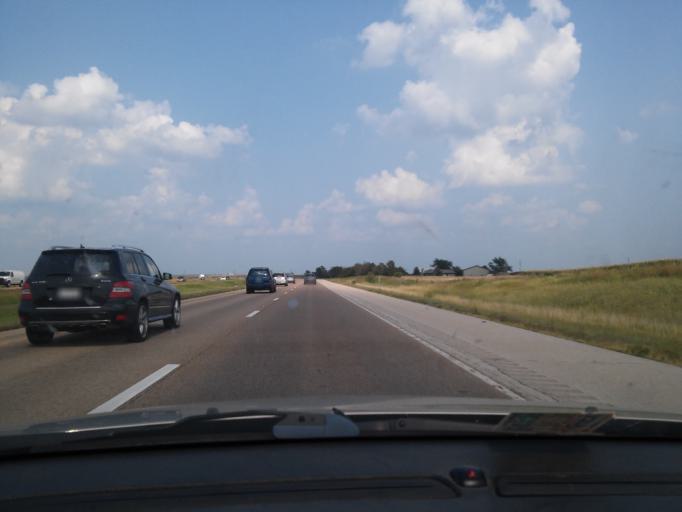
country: US
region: Illinois
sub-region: McLean County
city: Lexington
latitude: 40.6594
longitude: -88.7812
